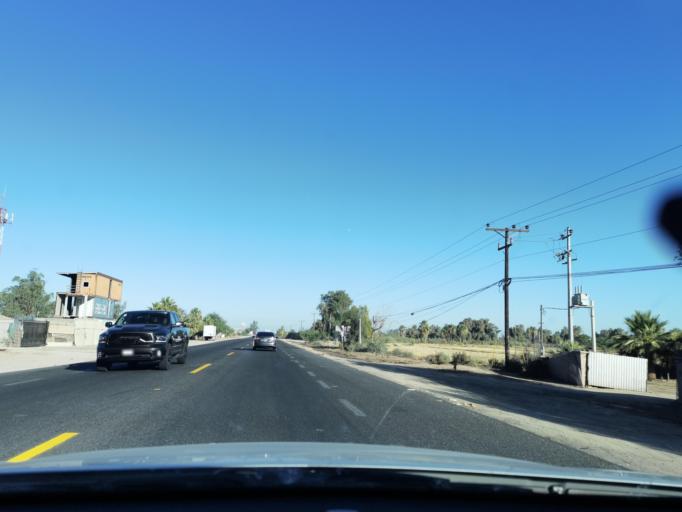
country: MX
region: Baja California
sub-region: Mexicali
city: Islas Agrarias Grupo A
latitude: 32.6438
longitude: -115.3132
